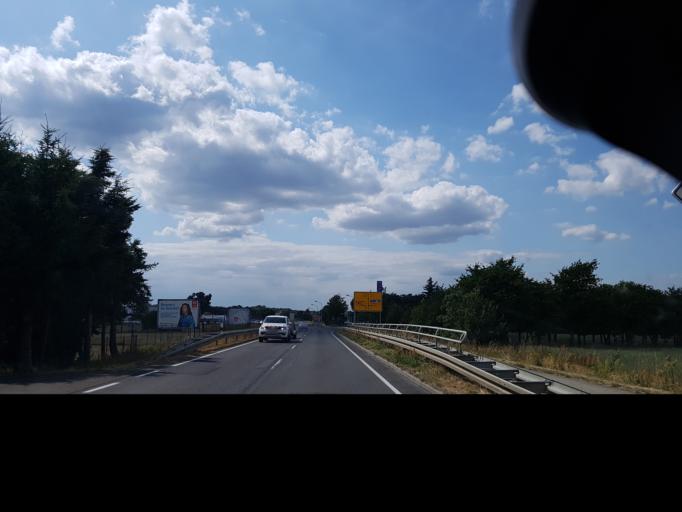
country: DE
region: Brandenburg
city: Cottbus
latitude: 51.7176
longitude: 14.2959
